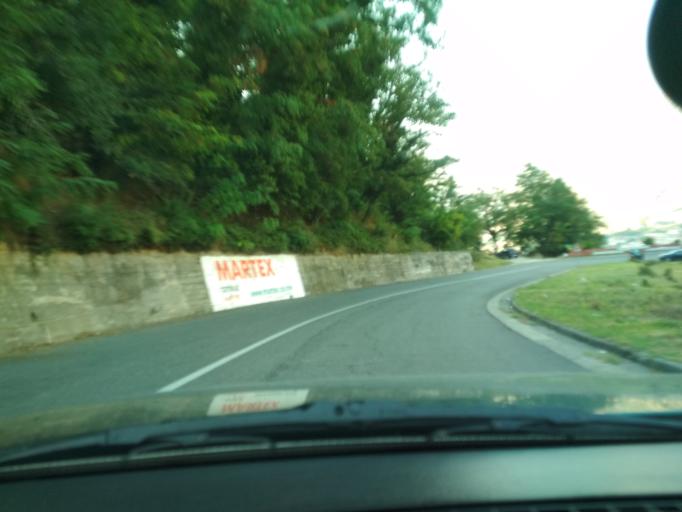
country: ME
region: Kotor
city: Kotor
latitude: 42.4214
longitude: 18.7584
